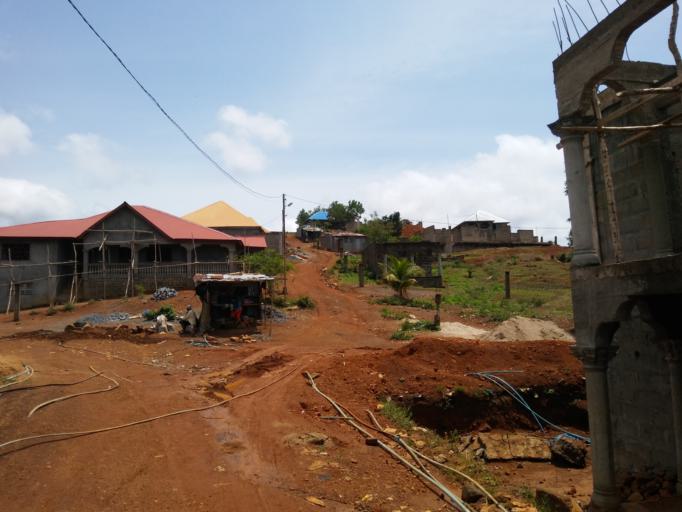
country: SL
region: Western Area
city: Hastings
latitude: 8.3903
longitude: -13.1651
